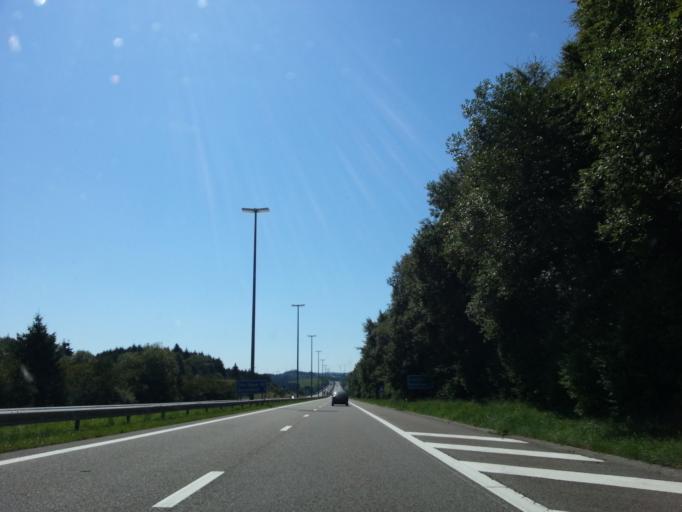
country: DE
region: Rheinland-Pfalz
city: Winterspelt
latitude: 50.2464
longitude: 6.1743
